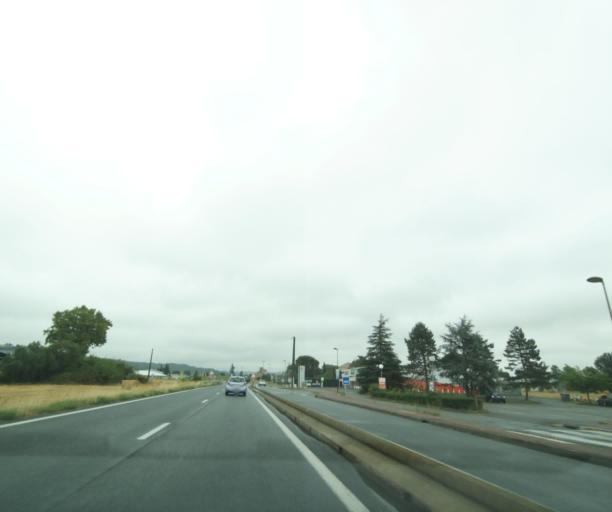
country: FR
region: Midi-Pyrenees
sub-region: Departement du Tarn
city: Albi
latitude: 43.9568
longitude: 2.1584
